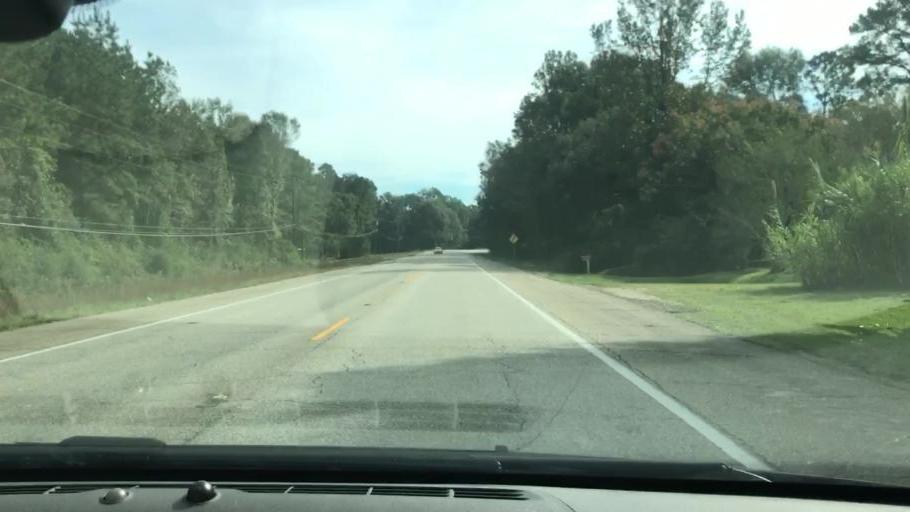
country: US
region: Mississippi
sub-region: Pearl River County
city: Nicholson
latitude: 30.5140
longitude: -89.8265
